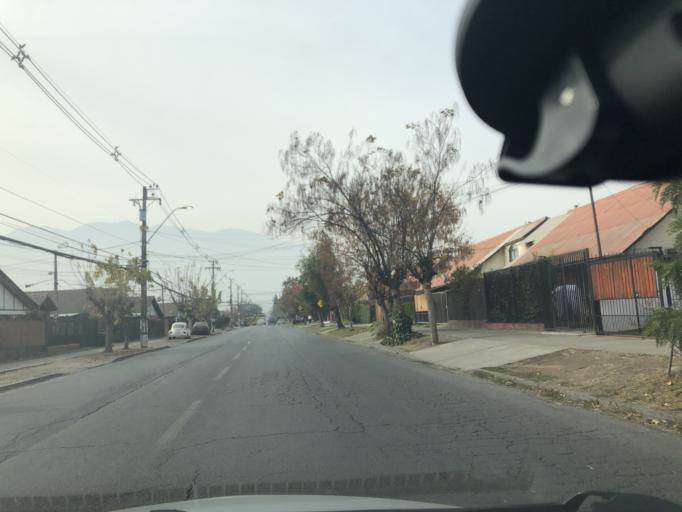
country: CL
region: Santiago Metropolitan
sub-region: Provincia de Cordillera
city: Puente Alto
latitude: -33.5688
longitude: -70.5777
